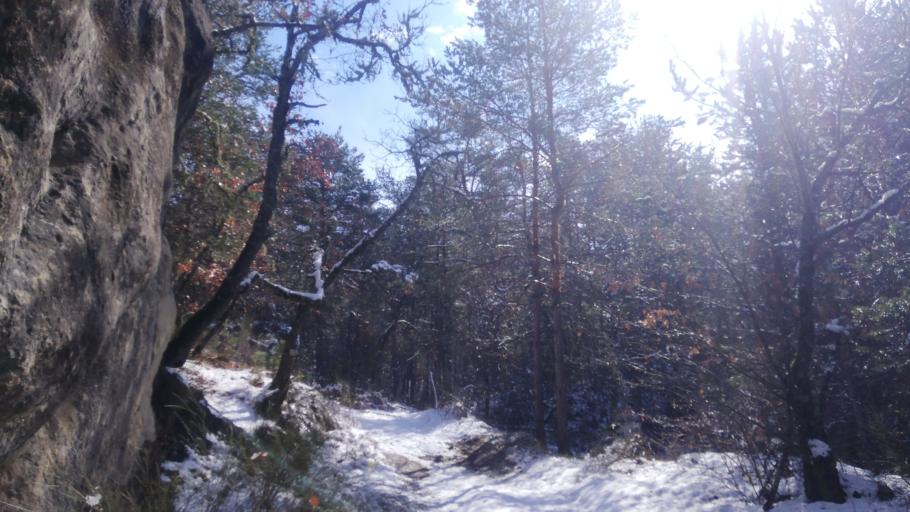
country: FR
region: Provence-Alpes-Cote d'Azur
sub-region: Departement des Alpes-de-Haute-Provence
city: Digne-les-Bains
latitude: 44.0435
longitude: 6.1984
